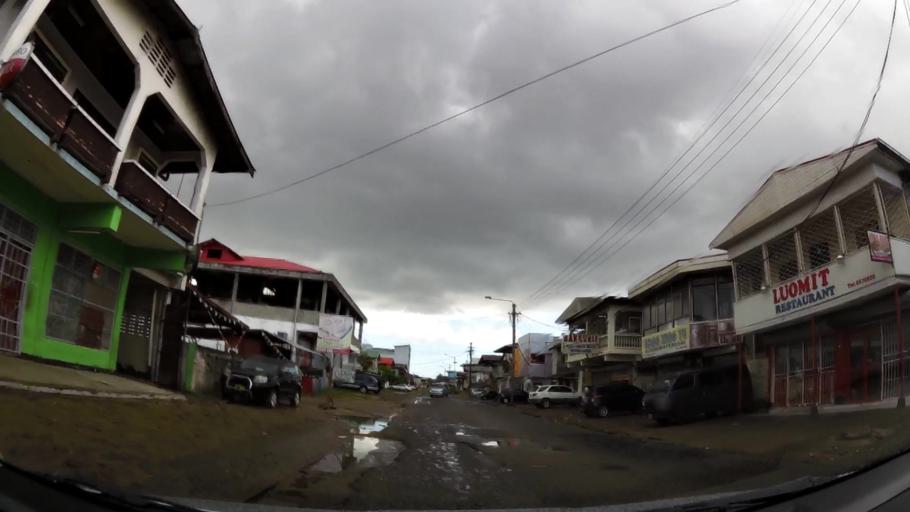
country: SR
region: Paramaribo
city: Paramaribo
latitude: 5.8167
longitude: -55.1746
